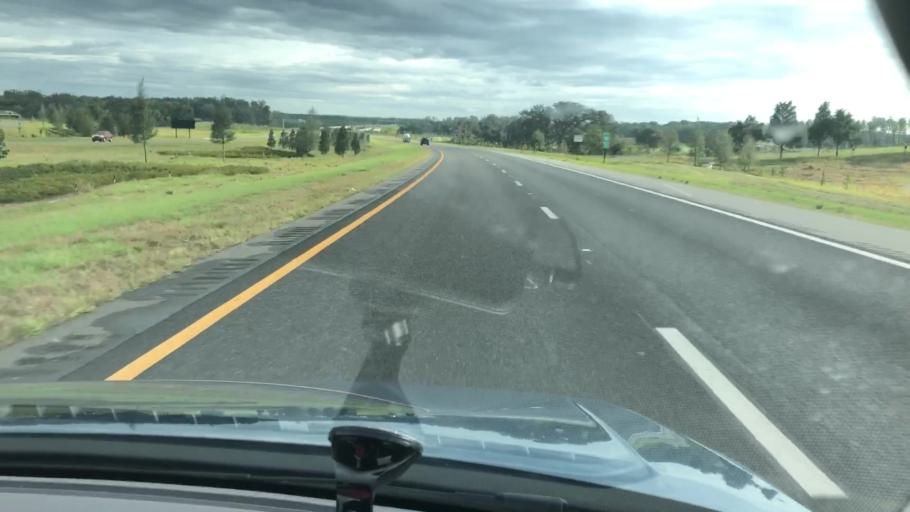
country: US
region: Florida
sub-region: Orange County
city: Zellwood
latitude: 28.7433
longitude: -81.5669
